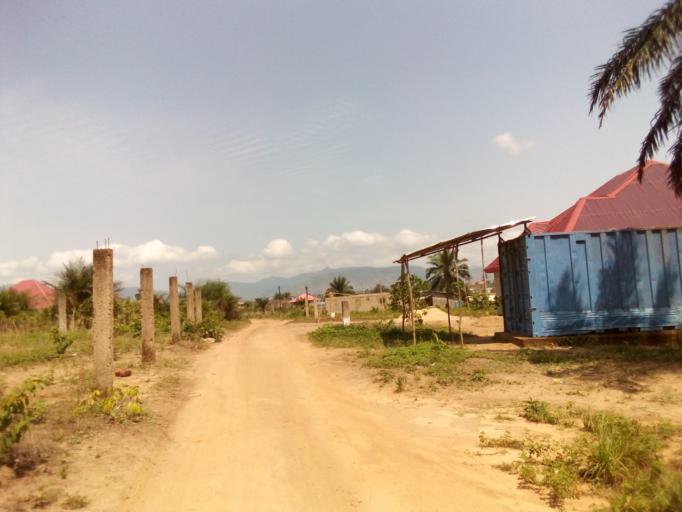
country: SL
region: Western Area
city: Waterloo
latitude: 8.3460
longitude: -13.0167
